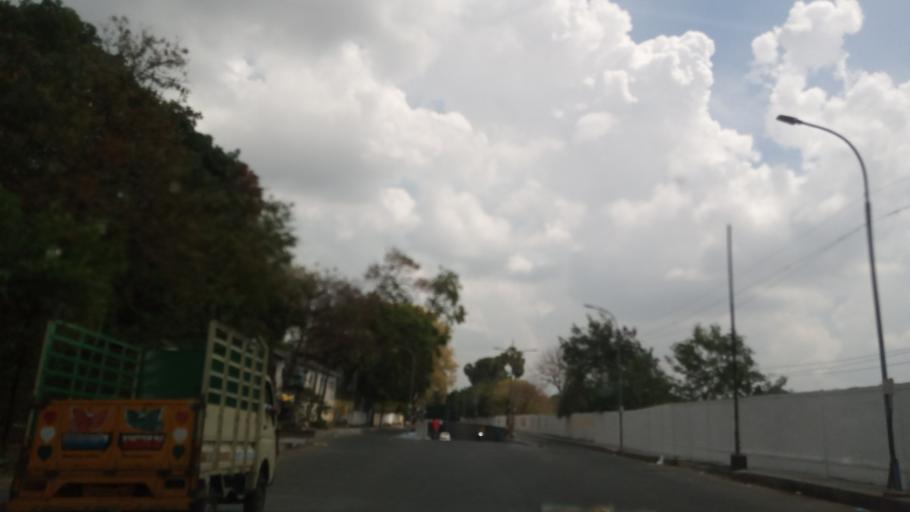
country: IN
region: Tamil Nadu
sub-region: Kancheepuram
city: Saint Thomas Mount
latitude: 12.9830
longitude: 80.1765
